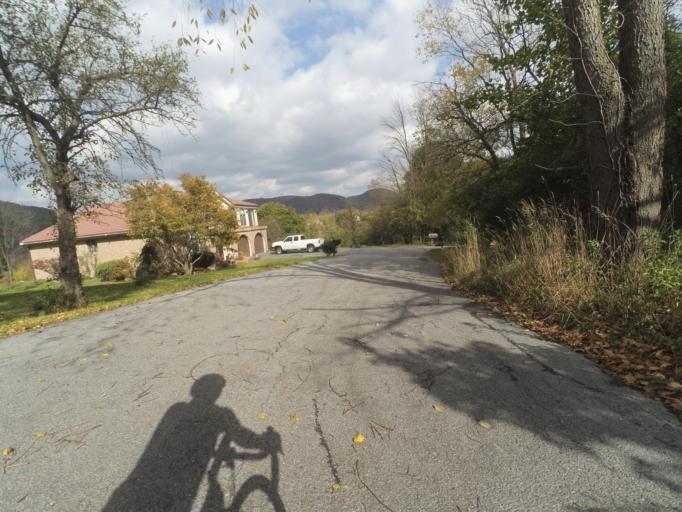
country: US
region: Pennsylvania
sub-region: Centre County
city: Bellefonte
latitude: 40.9137
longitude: -77.7855
